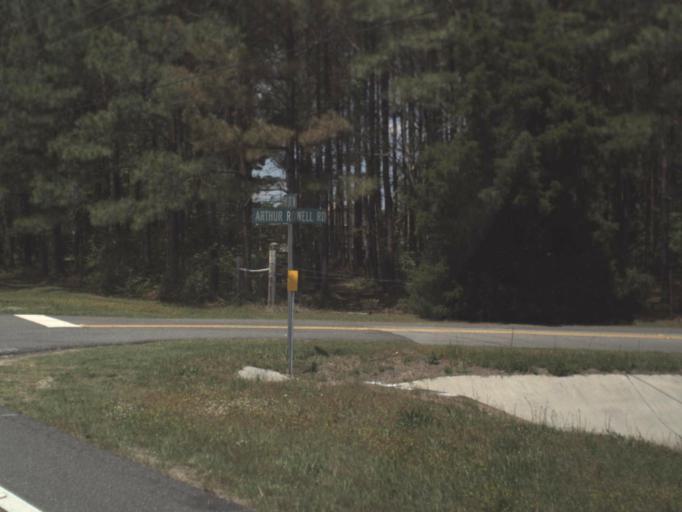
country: US
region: Alabama
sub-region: Escambia County
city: East Brewton
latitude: 30.9393
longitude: -87.0269
